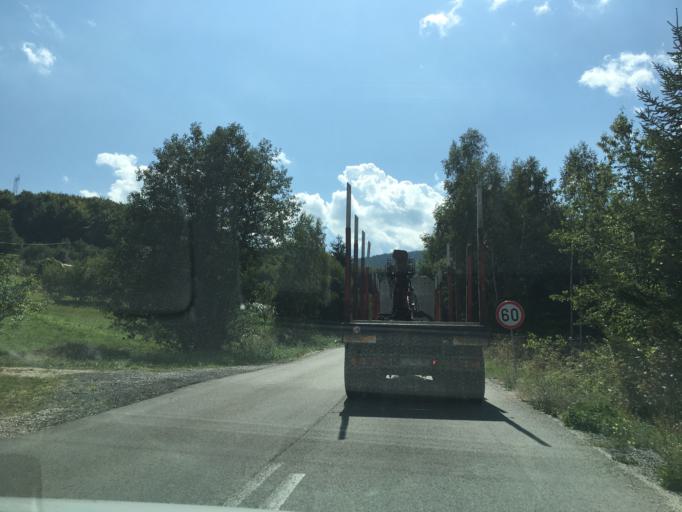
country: RS
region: Central Serbia
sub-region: Zlatiborski Okrug
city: Prijepolje
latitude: 43.3327
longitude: 19.5488
